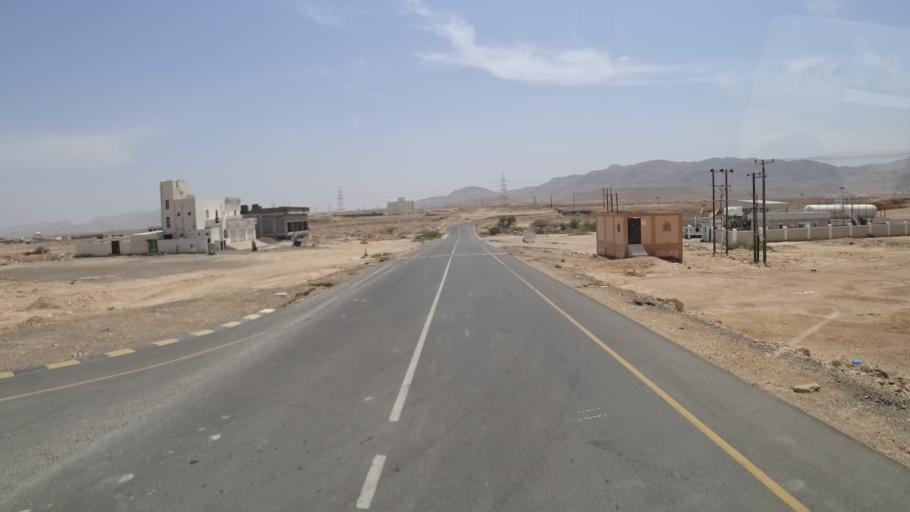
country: OM
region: Ash Sharqiyah
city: Sur
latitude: 22.5927
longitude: 59.4584
